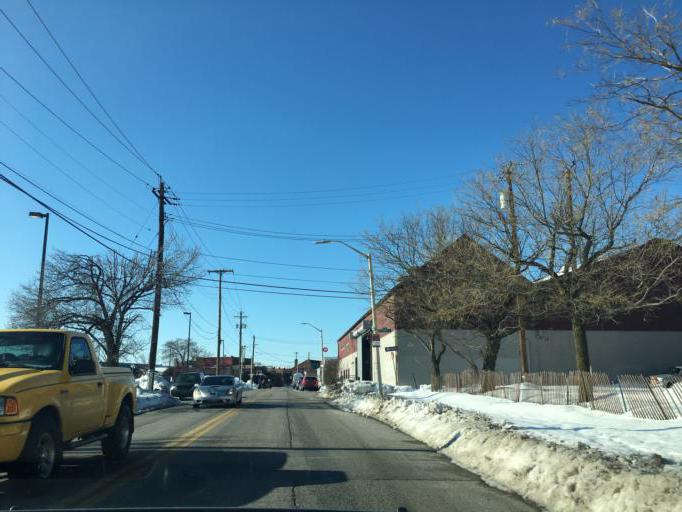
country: US
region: Maryland
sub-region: City of Baltimore
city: Baltimore
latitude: 39.2772
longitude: -76.6269
